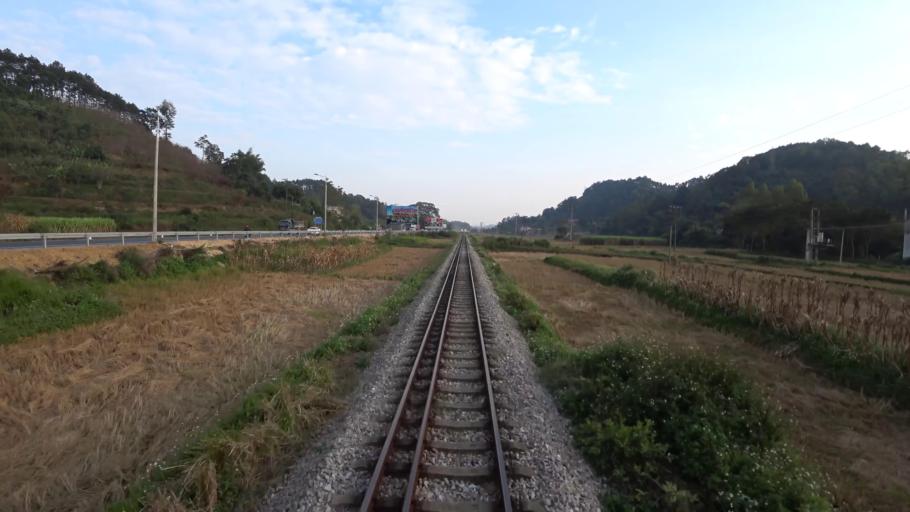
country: VN
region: Lang Son
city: Thi Tran Cao Loc
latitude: 21.9038
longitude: 106.7367
